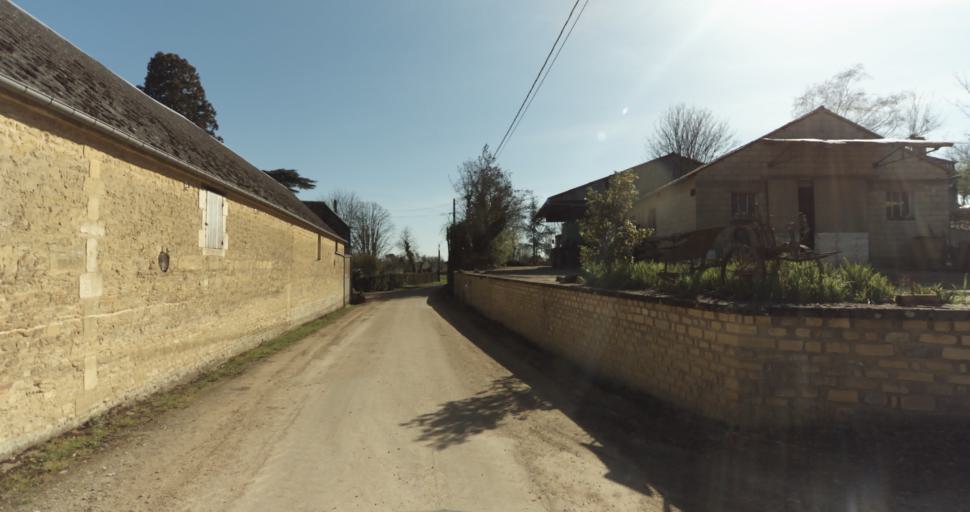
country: FR
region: Lower Normandy
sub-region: Departement du Calvados
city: Saint-Pierre-sur-Dives
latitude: 49.0177
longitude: 0.0146
